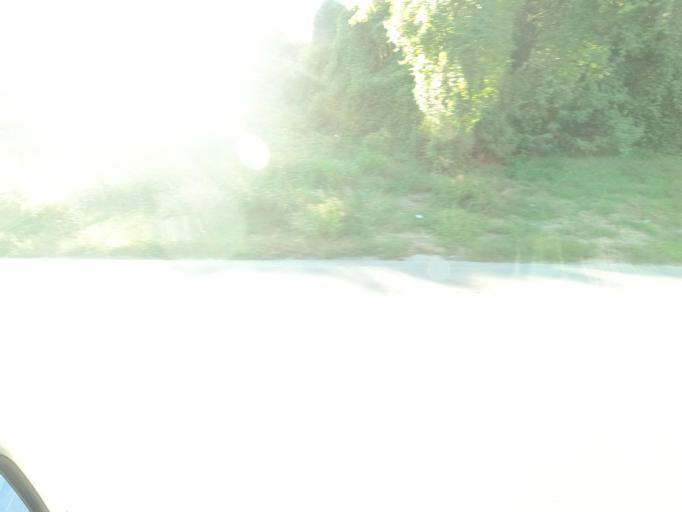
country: US
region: Tennessee
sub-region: Shelby County
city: New South Memphis
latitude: 35.1026
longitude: -90.0764
